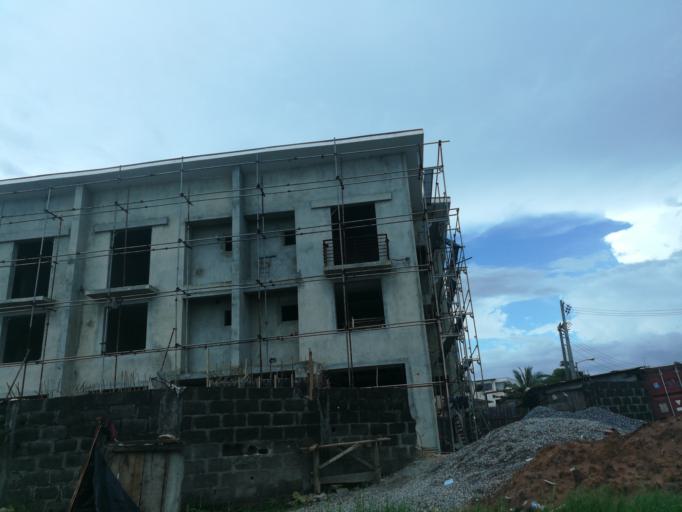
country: NG
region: Lagos
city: Ikoyi
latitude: 6.4390
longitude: 3.4786
